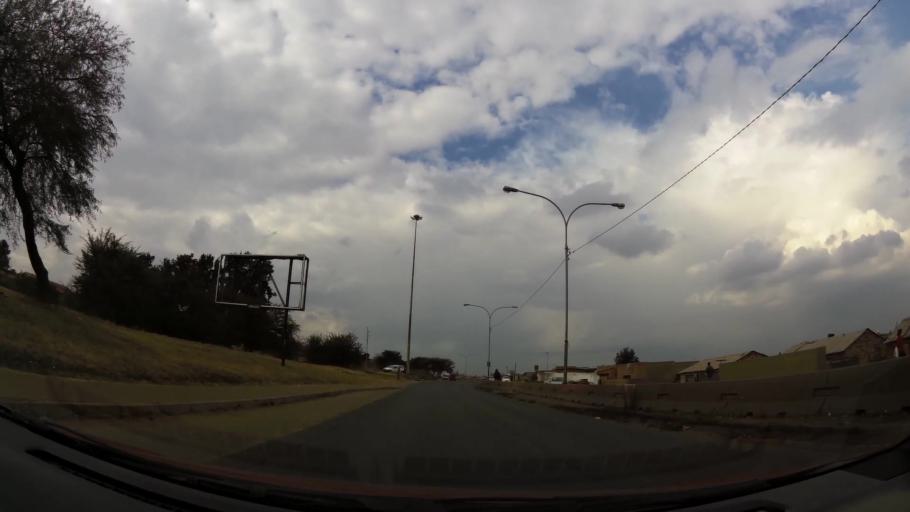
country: ZA
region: Gauteng
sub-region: City of Johannesburg Metropolitan Municipality
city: Soweto
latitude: -26.2347
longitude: 27.8665
